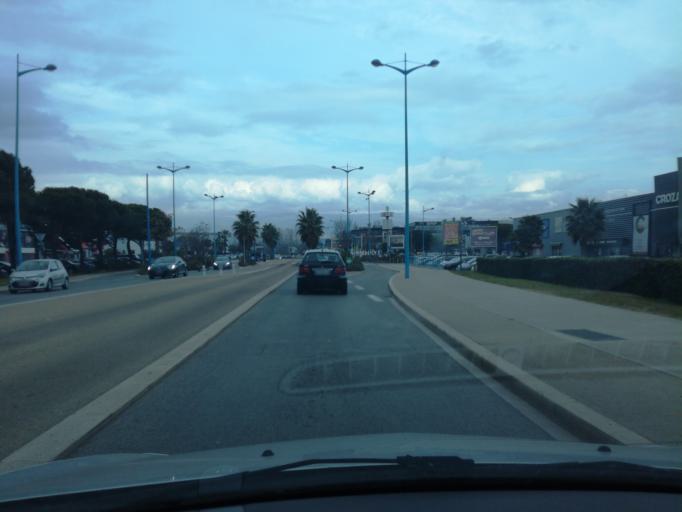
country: FR
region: Provence-Alpes-Cote d'Azur
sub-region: Departement des Alpes-Maritimes
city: Mandelieu-la-Napoule
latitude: 43.5537
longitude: 6.9548
